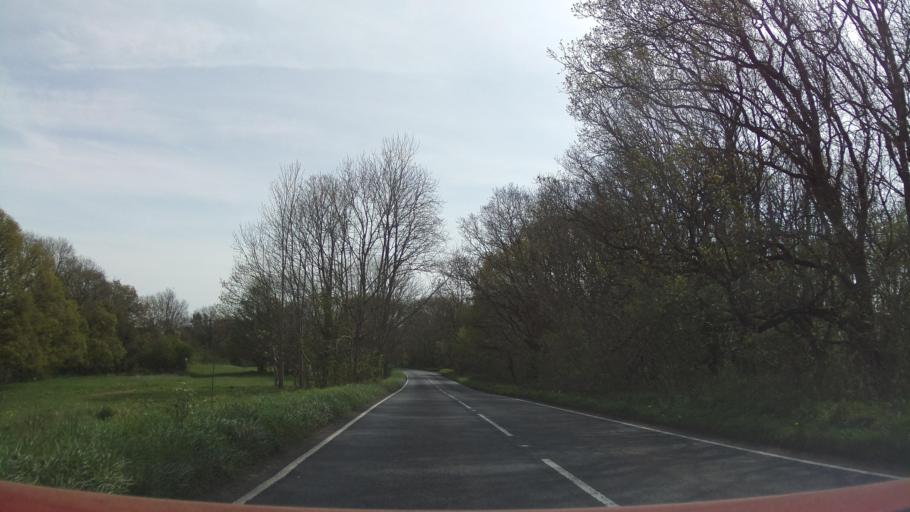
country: GB
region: England
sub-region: Somerset
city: Street
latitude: 51.1080
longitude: -2.7462
